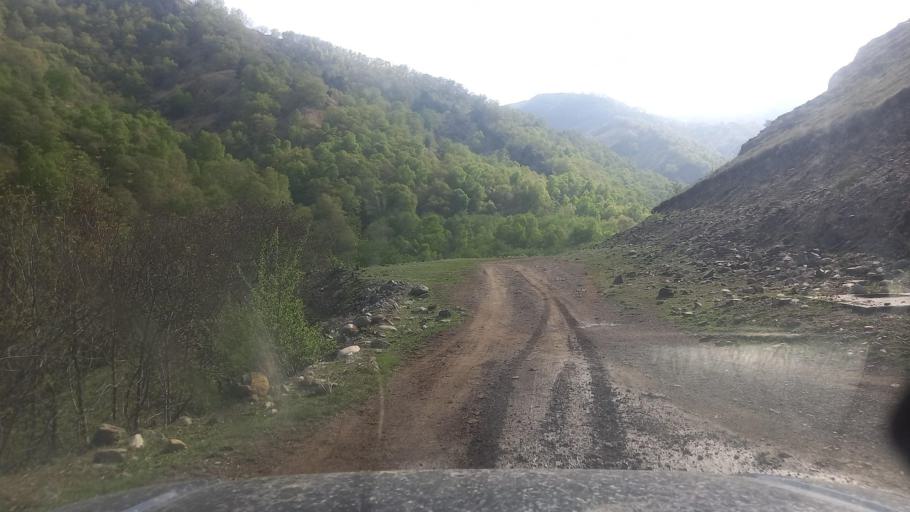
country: RU
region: Kabardino-Balkariya
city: Kamennomostskoye
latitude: 43.7196
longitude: 42.8898
